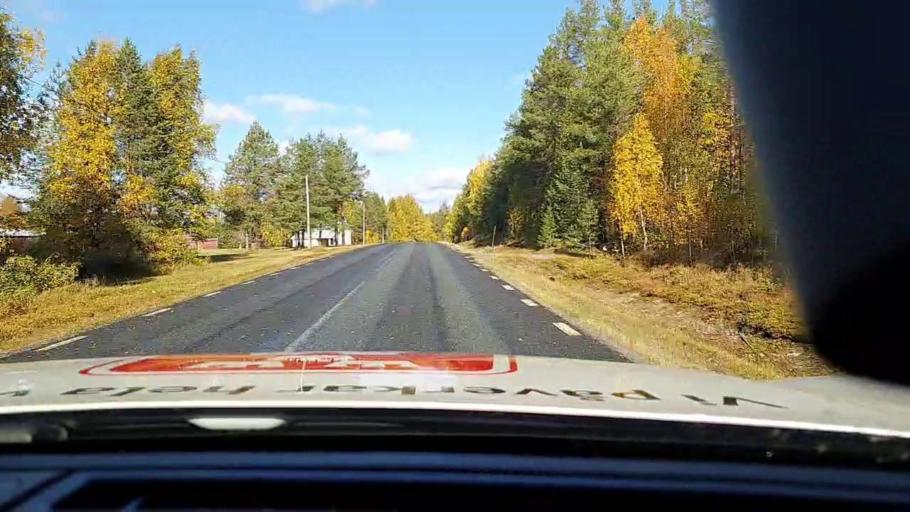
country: SE
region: Vaesterbotten
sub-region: Skelleftea Kommun
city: Langsele
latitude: 64.9984
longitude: 20.0904
